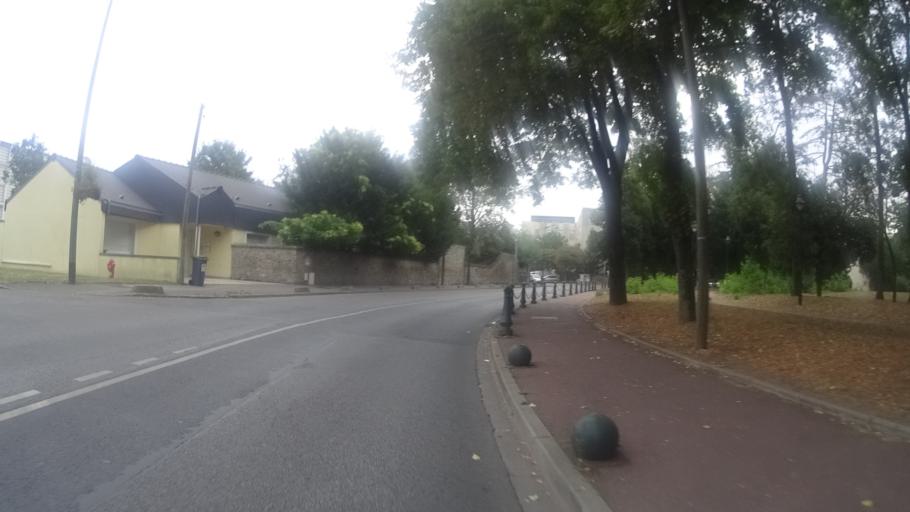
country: FR
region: Ile-de-France
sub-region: Departement de l'Essonne
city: Corbeil-Essonnes
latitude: 48.6071
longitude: 2.4694
